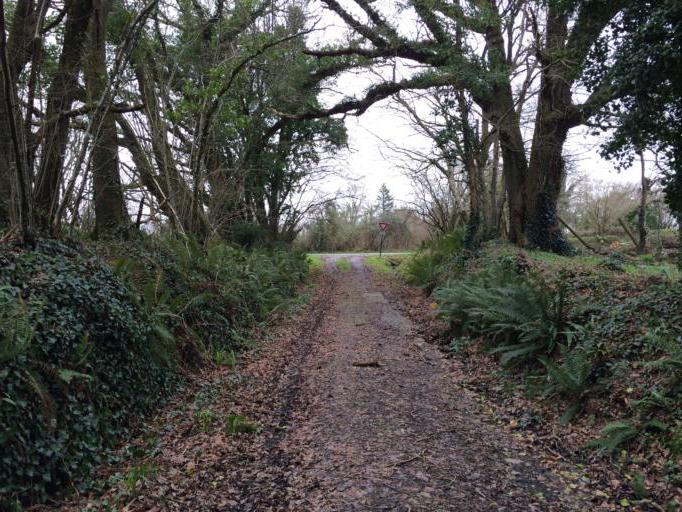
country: FR
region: Brittany
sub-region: Departement du Finistere
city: Hopital-Camfrout
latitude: 48.3272
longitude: -4.2668
